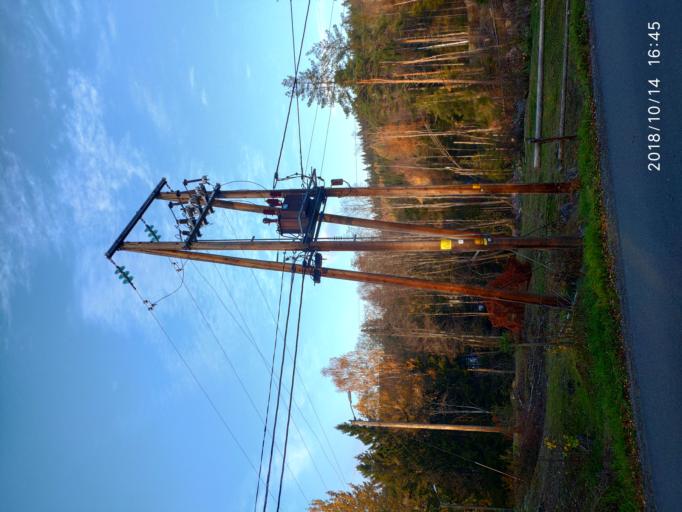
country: NO
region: Akershus
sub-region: Eidsvoll
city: Eidsvoll
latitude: 60.2782
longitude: 11.2561
